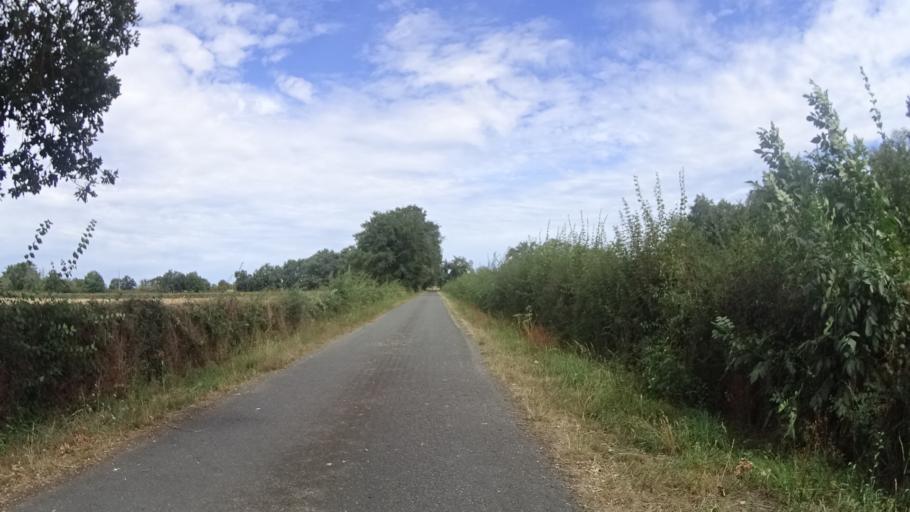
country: FR
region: Auvergne
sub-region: Departement de l'Allier
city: Beaulon
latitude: 46.6478
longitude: 3.6671
